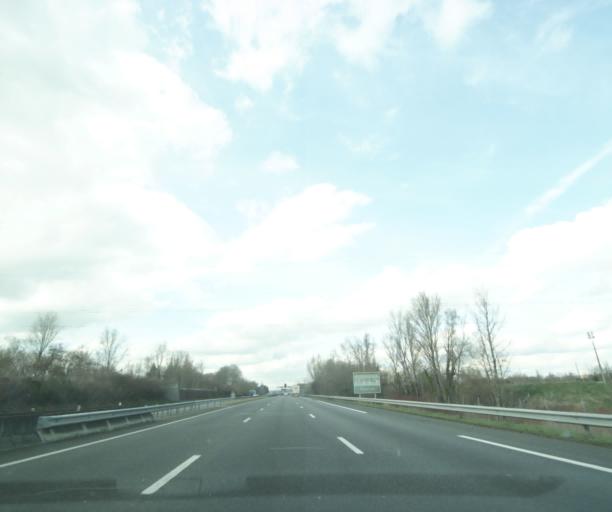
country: FR
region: Midi-Pyrenees
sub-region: Departement de la Haute-Garonne
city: Labege
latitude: 43.5222
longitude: 1.5211
